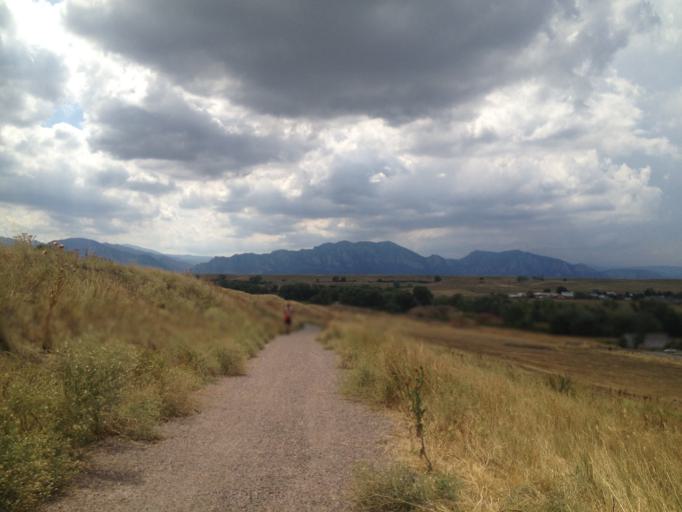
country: US
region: Colorado
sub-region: Boulder County
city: Superior
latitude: 39.9480
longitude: -105.1664
